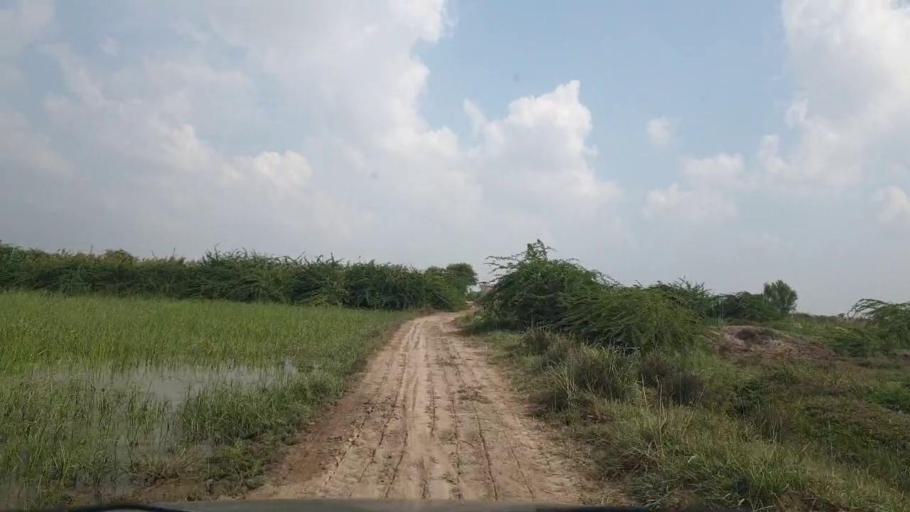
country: PK
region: Sindh
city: Badin
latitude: 24.5328
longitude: 68.6413
